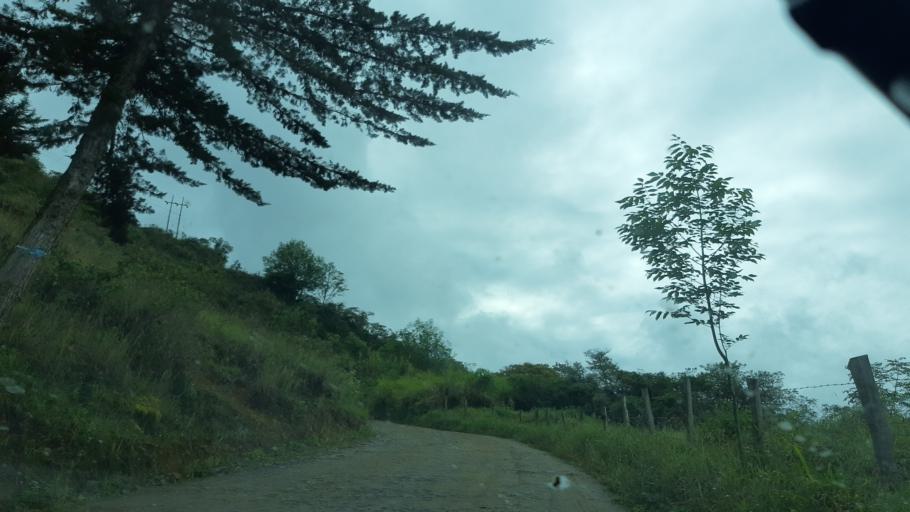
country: CO
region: Boyaca
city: Guateque
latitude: 5.0331
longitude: -73.4431
